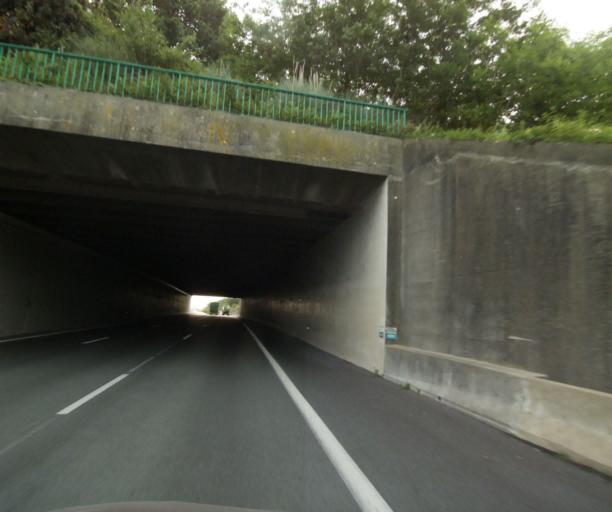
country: FR
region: Aquitaine
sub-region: Departement des Pyrenees-Atlantiques
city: Guethary
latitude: 43.4169
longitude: -1.6049
